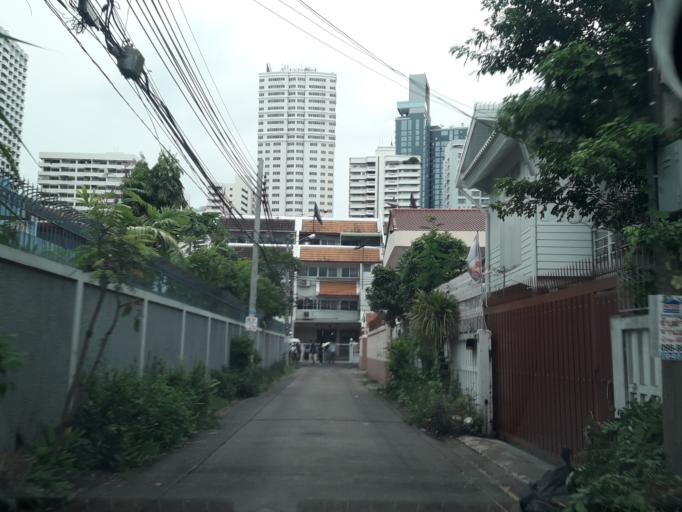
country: TH
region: Bangkok
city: Khlong Toei
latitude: 13.7354
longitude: 100.5548
